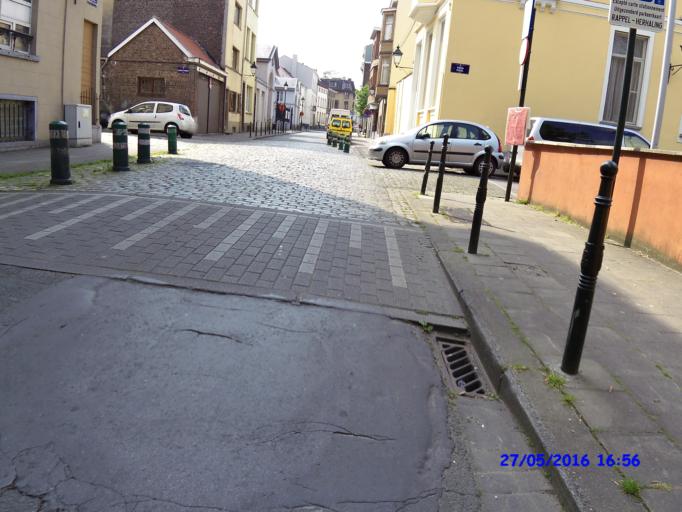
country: BE
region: Brussels Capital
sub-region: Bruxelles-Capitale
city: Brussels
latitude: 50.8770
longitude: 4.3601
